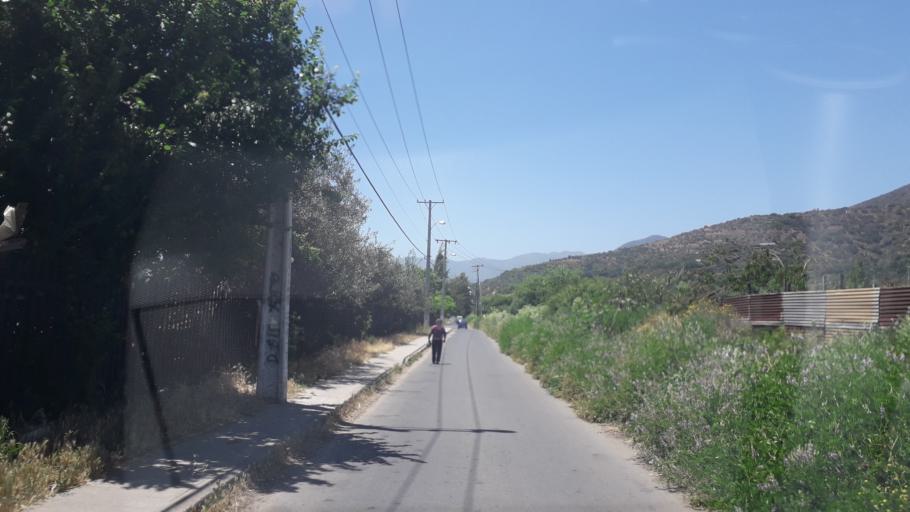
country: CL
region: Valparaiso
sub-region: Provincia de Quillota
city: Quillota
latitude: -32.9369
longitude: -71.2707
